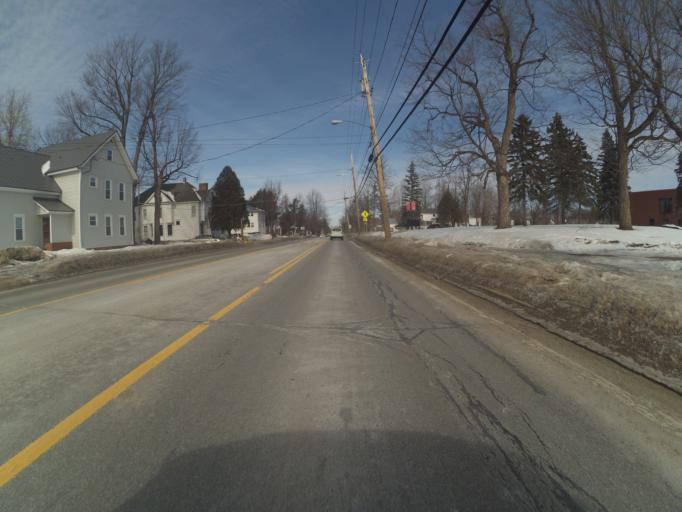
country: US
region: New York
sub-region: St. Lawrence County
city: Potsdam
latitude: 44.6634
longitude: -74.9782
